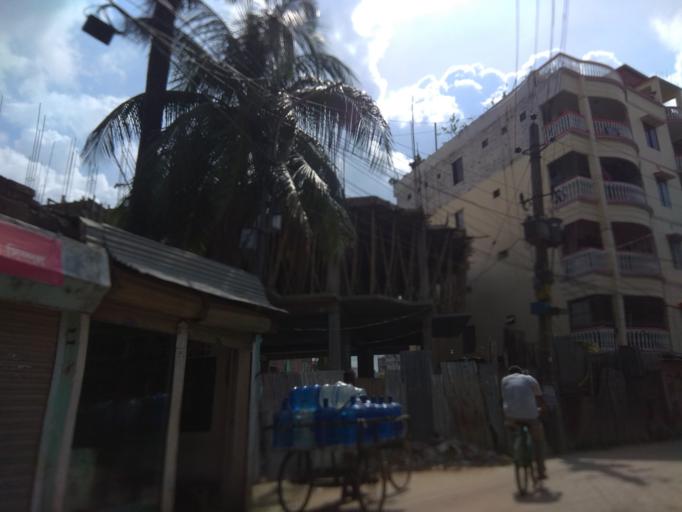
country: BD
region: Dhaka
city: Tungi
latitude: 23.8136
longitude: 90.3908
